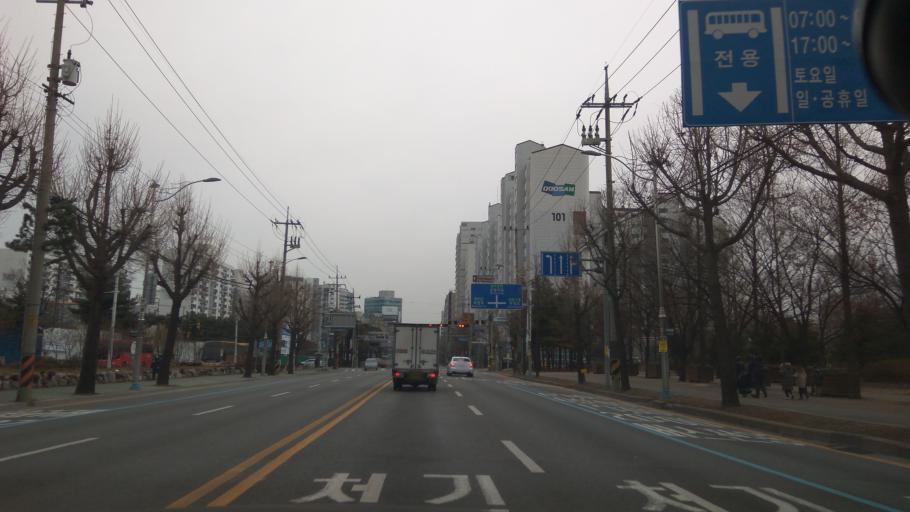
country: KR
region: Incheon
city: Incheon
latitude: 37.4911
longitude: 126.7149
